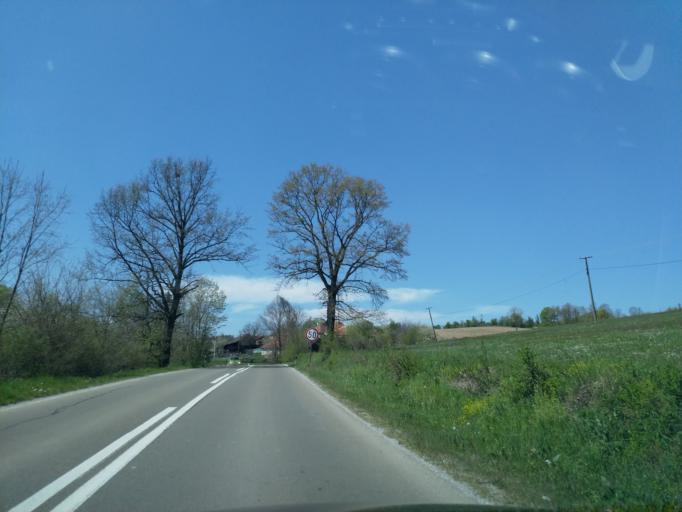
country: RS
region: Central Serbia
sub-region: Belgrade
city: Lazarevac
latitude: 44.3548
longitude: 20.3678
